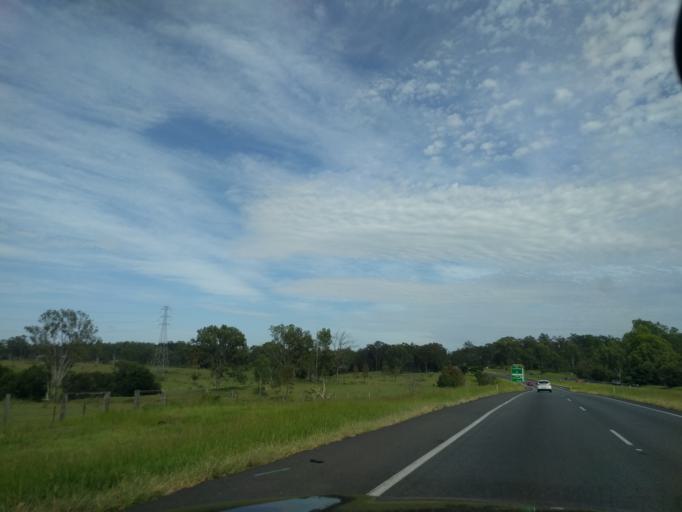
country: AU
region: Queensland
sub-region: Ipswich
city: North Booval
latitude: -27.5777
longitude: 152.8049
